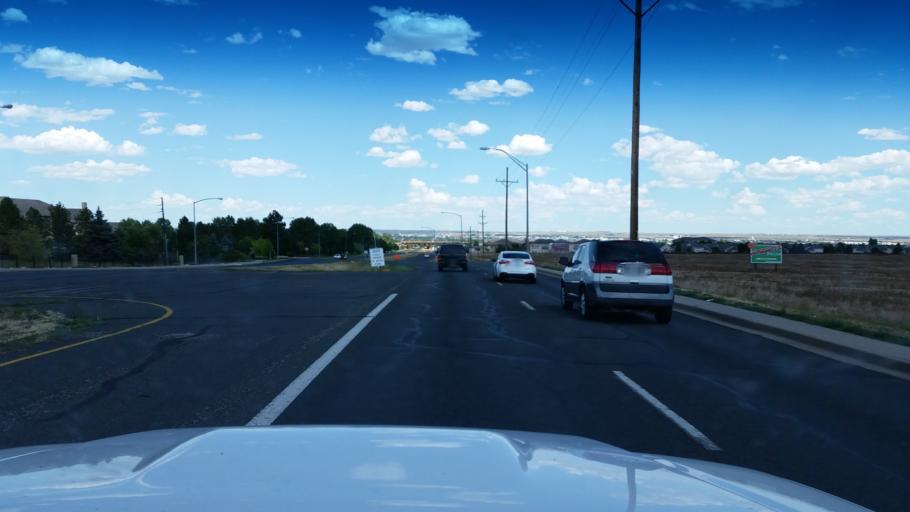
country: US
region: Colorado
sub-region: Adams County
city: Thornton
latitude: 39.8848
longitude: -104.9560
